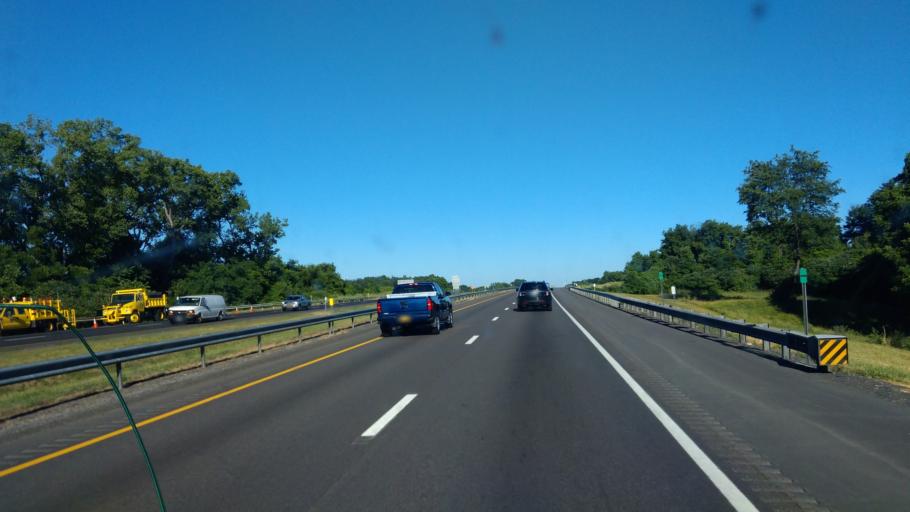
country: US
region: New York
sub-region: Ontario County
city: Phelps
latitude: 42.9552
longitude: -77.0033
